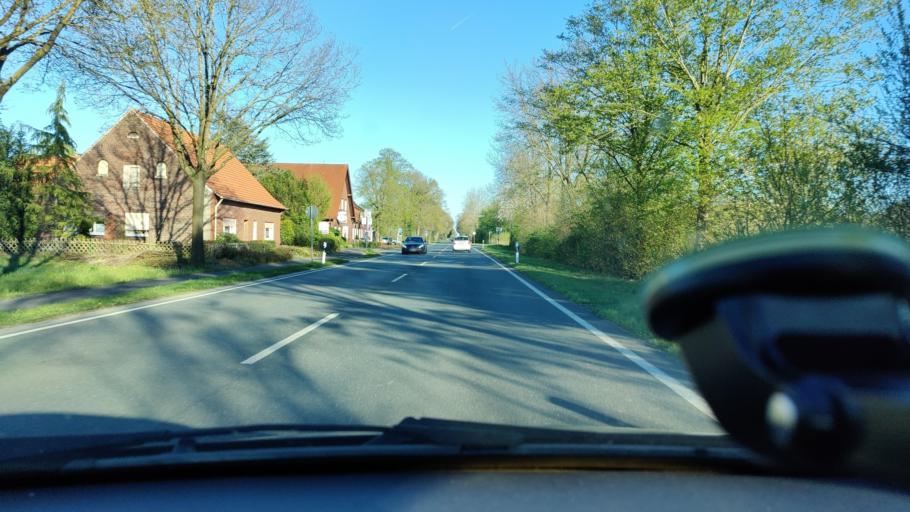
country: DE
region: North Rhine-Westphalia
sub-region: Regierungsbezirk Munster
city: Ahaus
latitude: 52.0607
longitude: 7.0342
